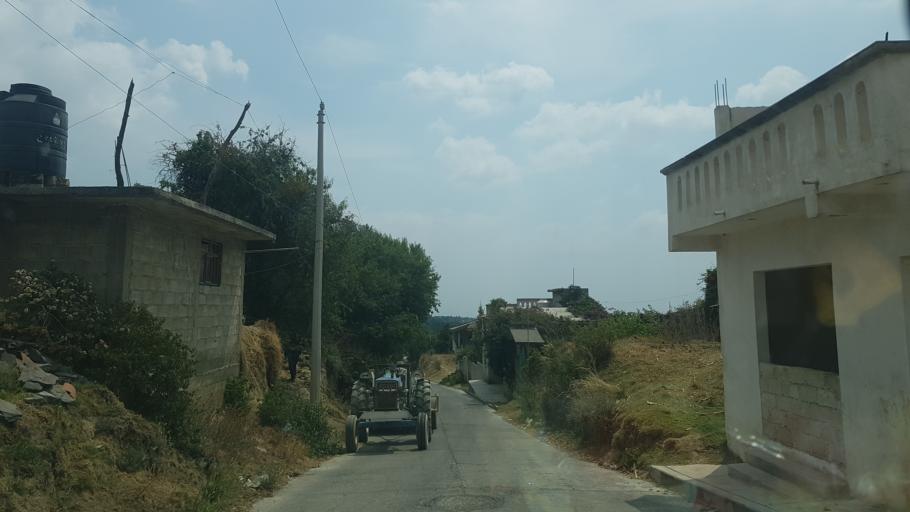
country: MX
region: Puebla
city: Domingo Arenas
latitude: 19.1375
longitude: -98.4810
